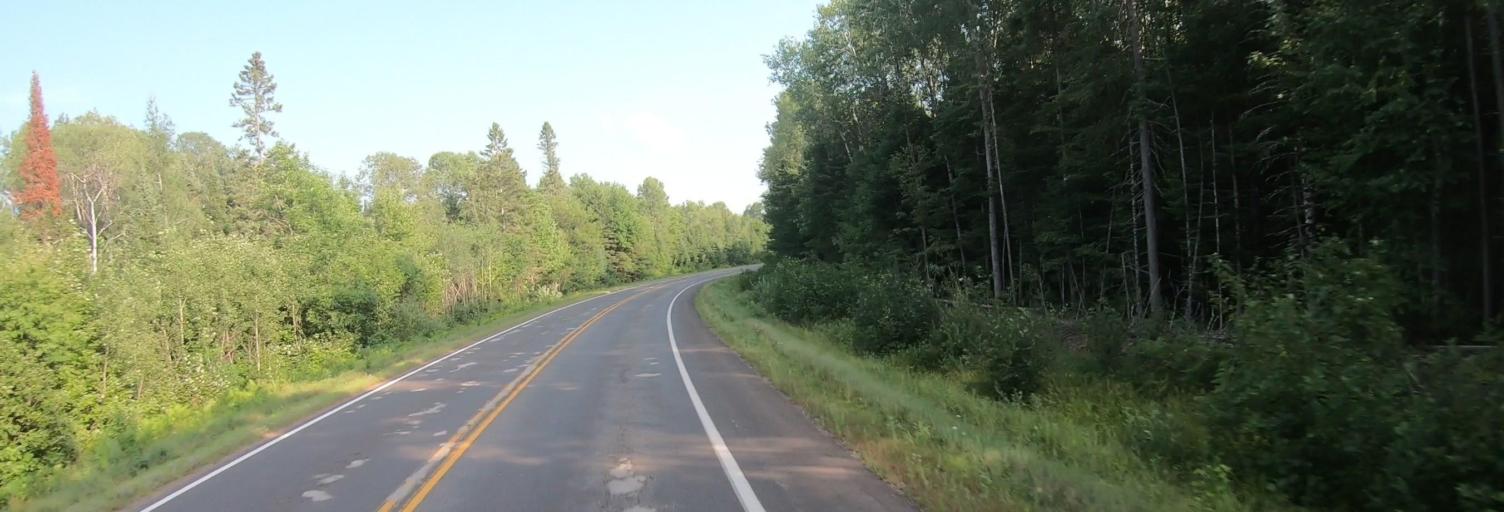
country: US
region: Wisconsin
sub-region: Ashland County
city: Ashland
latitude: 46.2540
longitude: -90.8319
